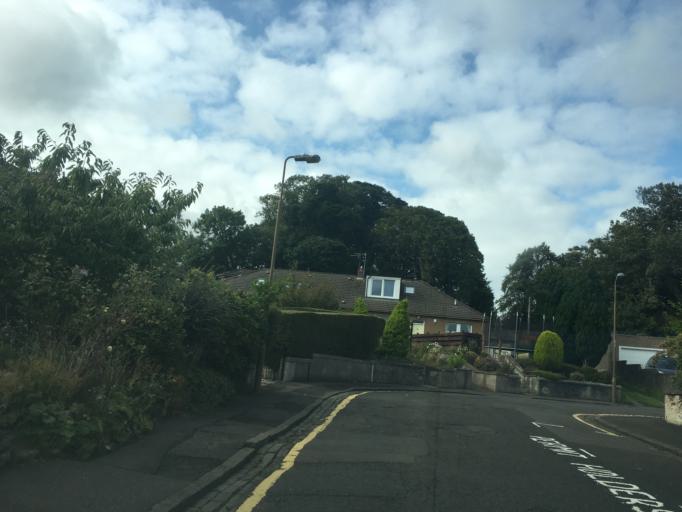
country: GB
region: Scotland
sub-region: Edinburgh
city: Edinburgh
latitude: 55.9320
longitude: -3.1867
